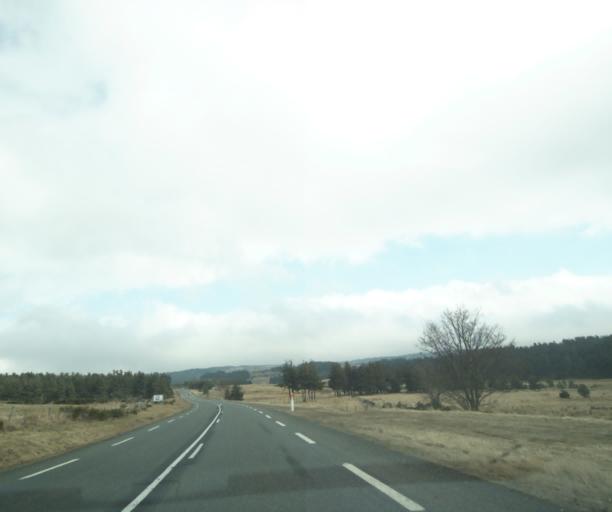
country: FR
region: Languedoc-Roussillon
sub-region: Departement de la Lozere
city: Langogne
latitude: 44.6413
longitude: 3.7198
